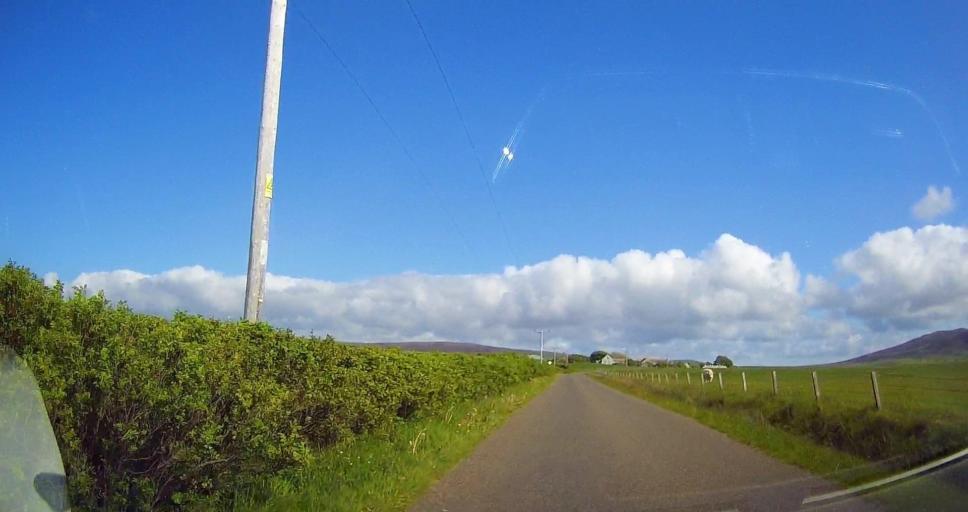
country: GB
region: Scotland
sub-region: Orkney Islands
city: Stromness
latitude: 58.9964
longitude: -3.1630
